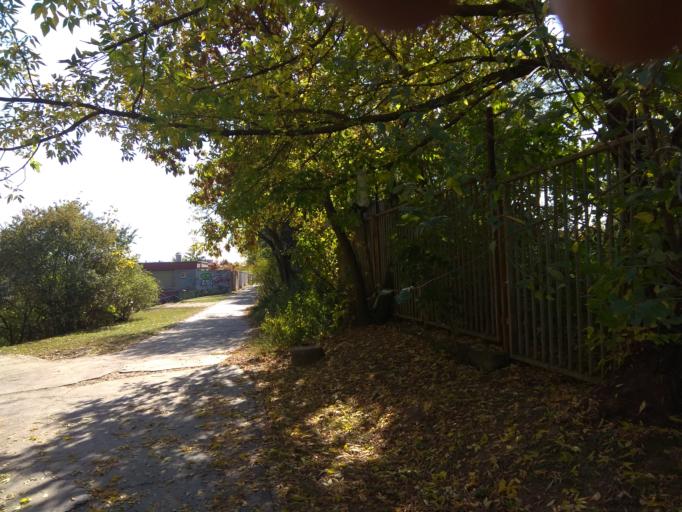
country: SK
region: Kosicky
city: Kosice
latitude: 48.7227
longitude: 21.2426
